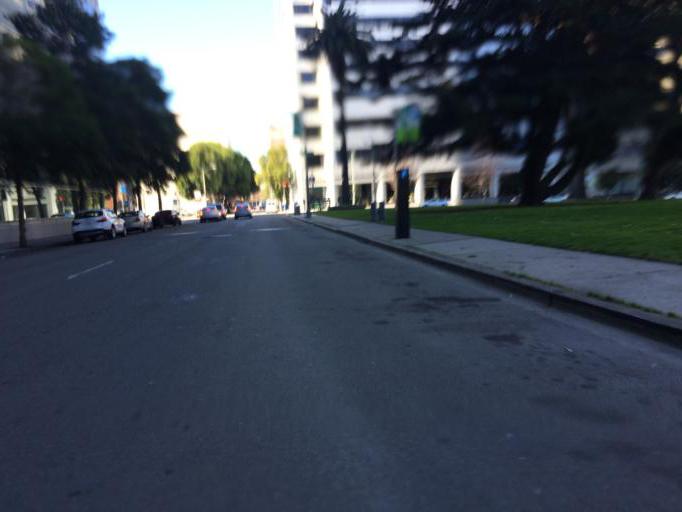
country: US
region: California
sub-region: Alameda County
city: Oakland
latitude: 37.8061
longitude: -122.2646
